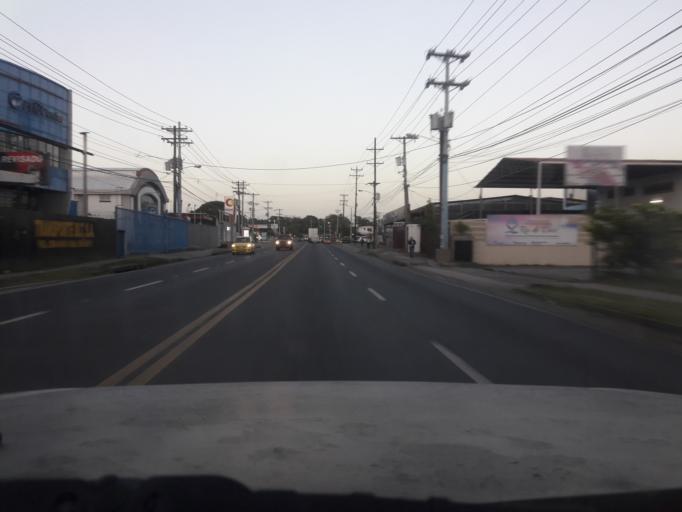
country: PA
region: Panama
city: San Miguelito
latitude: 9.0487
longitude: -79.4390
